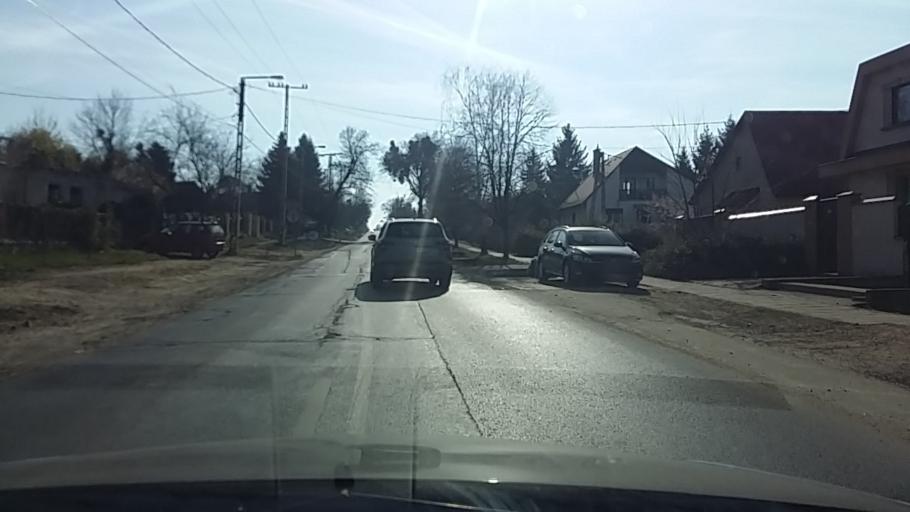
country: HU
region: Pest
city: Godollo
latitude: 47.5884
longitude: 19.3622
